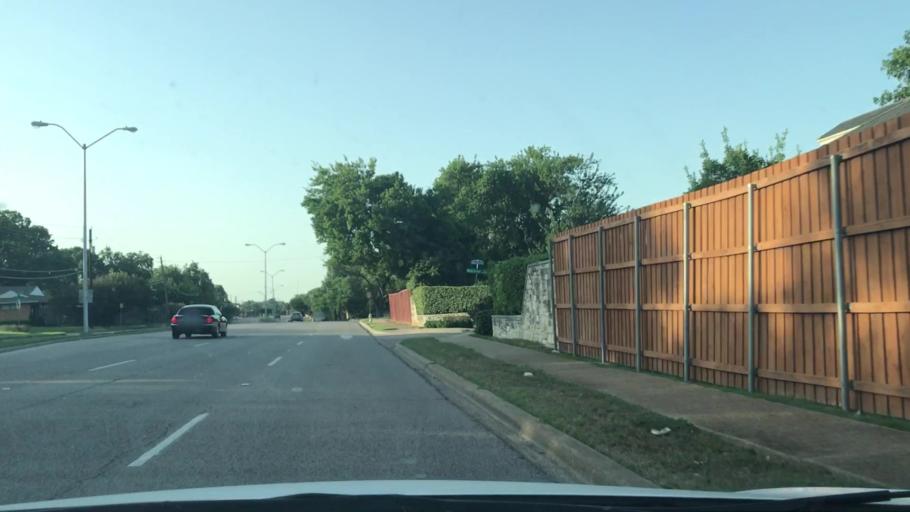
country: US
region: Texas
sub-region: Dallas County
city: Garland
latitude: 32.8734
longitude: -96.6999
